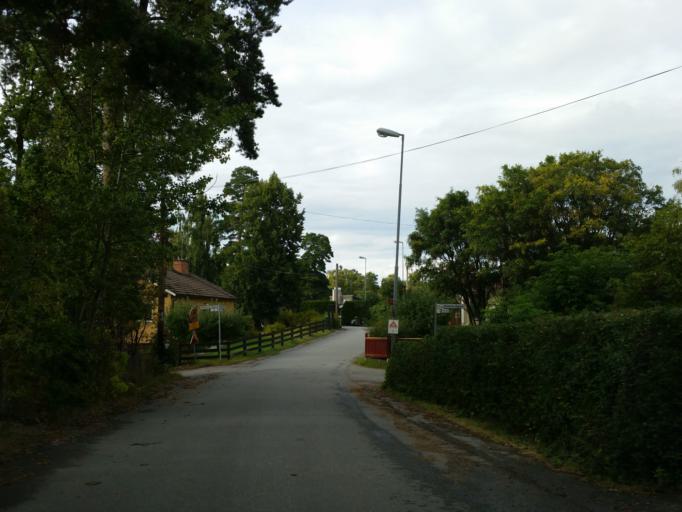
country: SE
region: Stockholm
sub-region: Sollentuna Kommun
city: Sollentuna
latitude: 59.4590
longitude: 17.9294
